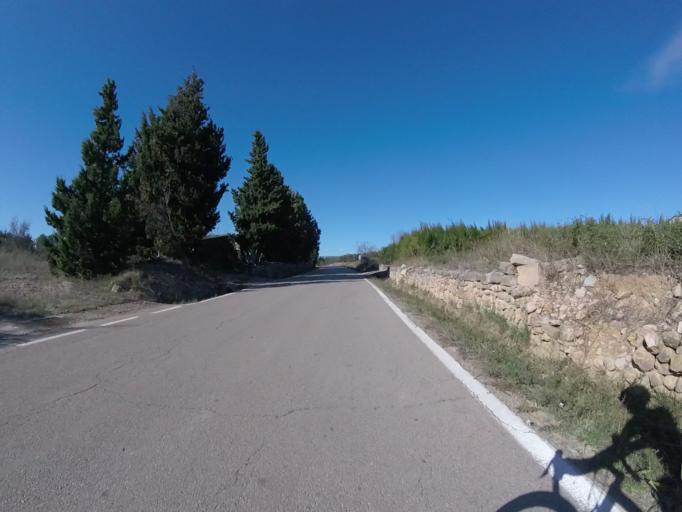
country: ES
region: Valencia
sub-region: Provincia de Castello
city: Chert/Xert
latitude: 40.4649
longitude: 0.1728
